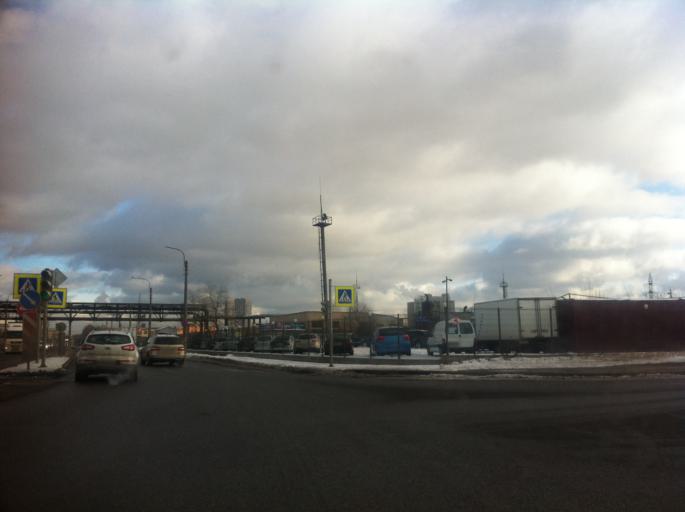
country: RU
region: St.-Petersburg
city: Avtovo
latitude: 59.8681
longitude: 30.2375
